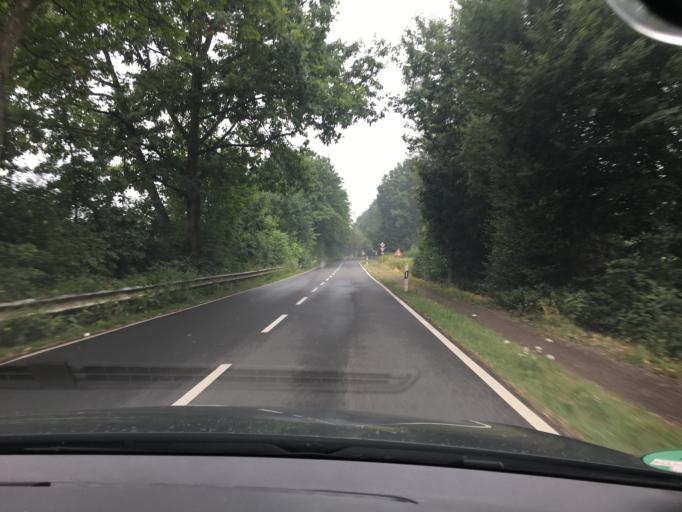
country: DE
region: North Rhine-Westphalia
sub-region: Regierungsbezirk Koln
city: Niederzier
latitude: 50.9064
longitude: 6.4401
